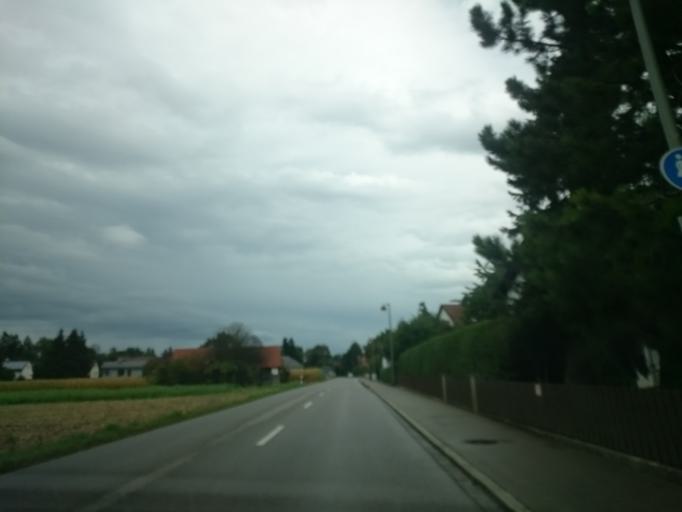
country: DE
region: Bavaria
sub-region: Swabia
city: Graben
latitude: 48.1850
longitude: 10.8178
